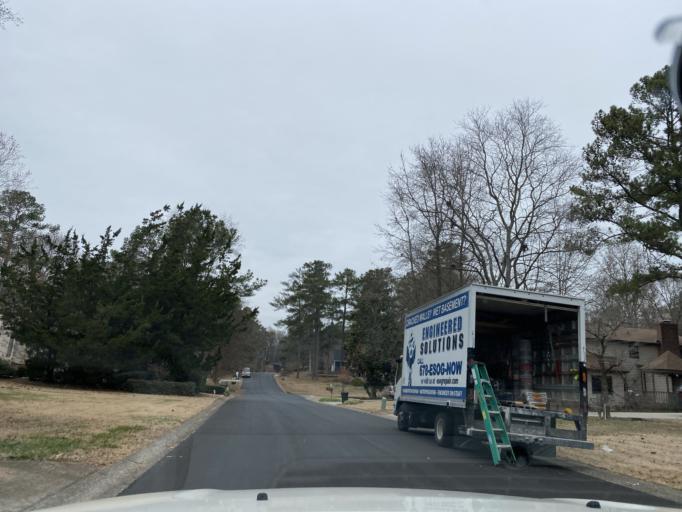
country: US
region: Georgia
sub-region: Cobb County
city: Fair Oaks
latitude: 33.9143
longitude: -84.5669
